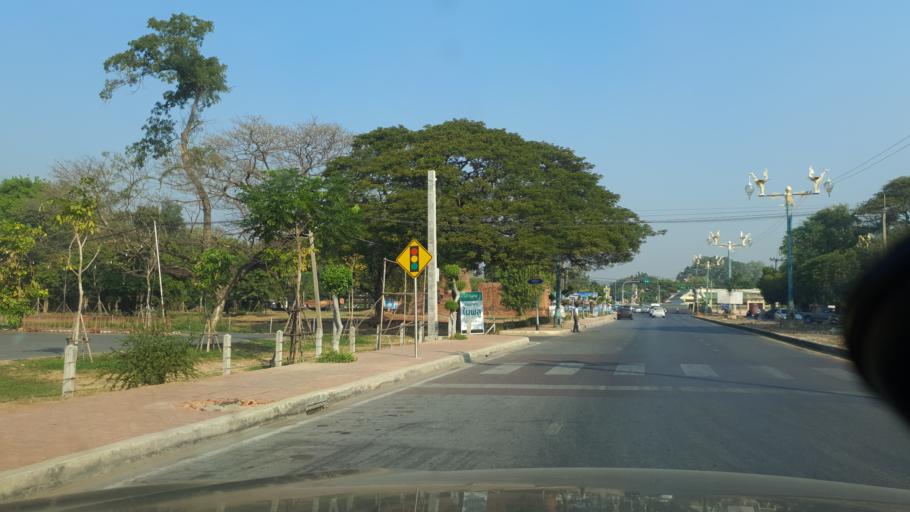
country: TH
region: Phra Nakhon Si Ayutthaya
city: Phra Nakhon Si Ayutthaya
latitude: 14.3596
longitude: 100.5685
